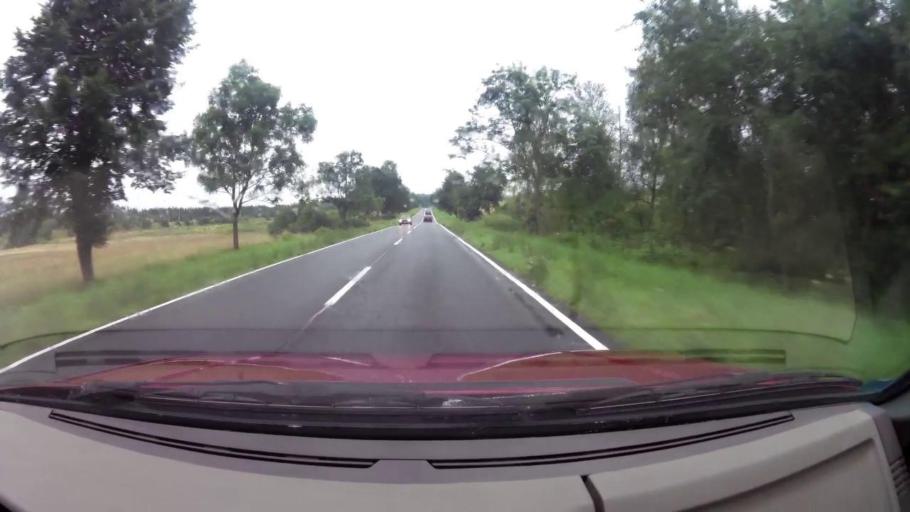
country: PL
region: West Pomeranian Voivodeship
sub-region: Powiat stargardzki
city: Marianowo
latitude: 53.4261
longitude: 15.2864
